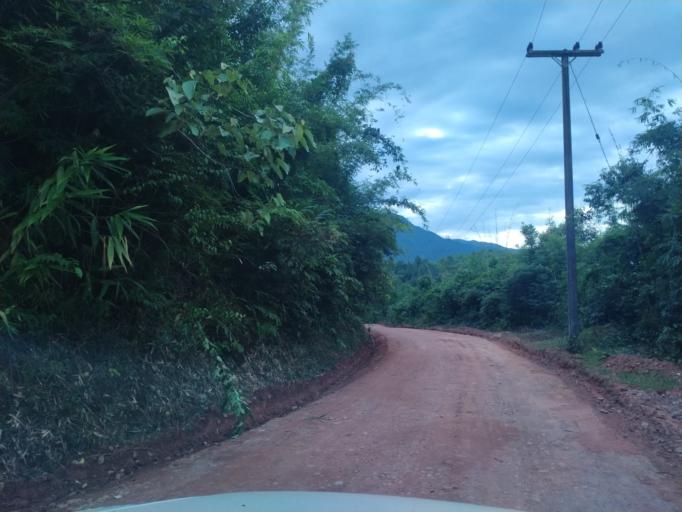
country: TH
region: Nong Khai
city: Rattanawapi
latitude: 18.5437
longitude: 102.9040
